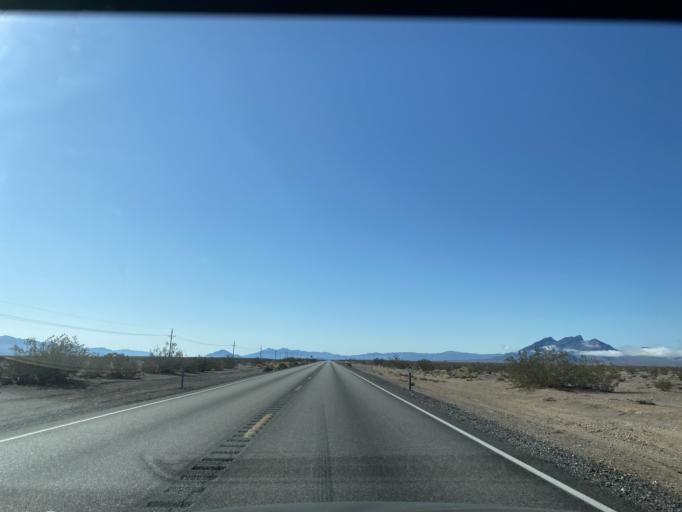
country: US
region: Nevada
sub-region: Nye County
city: Pahrump
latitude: 36.4879
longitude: -116.4215
